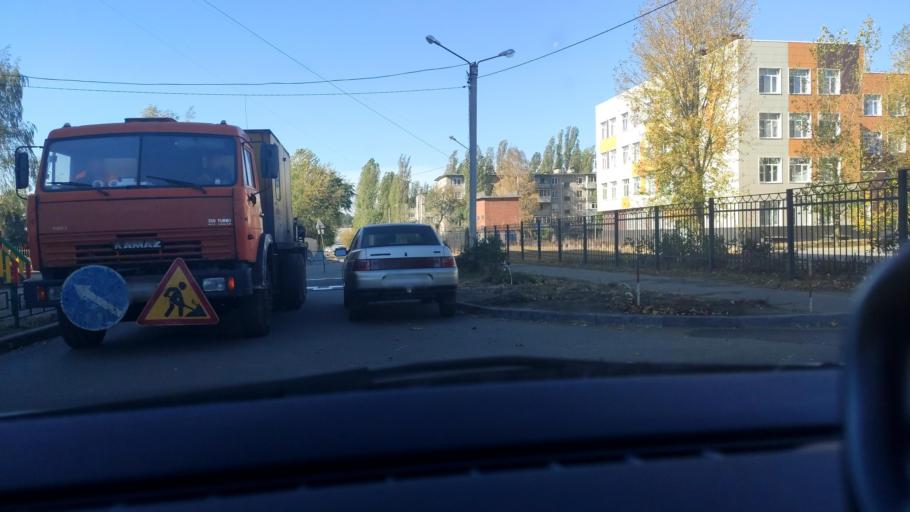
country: RU
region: Voronezj
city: Pridonskoy
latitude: 51.6254
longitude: 39.0722
